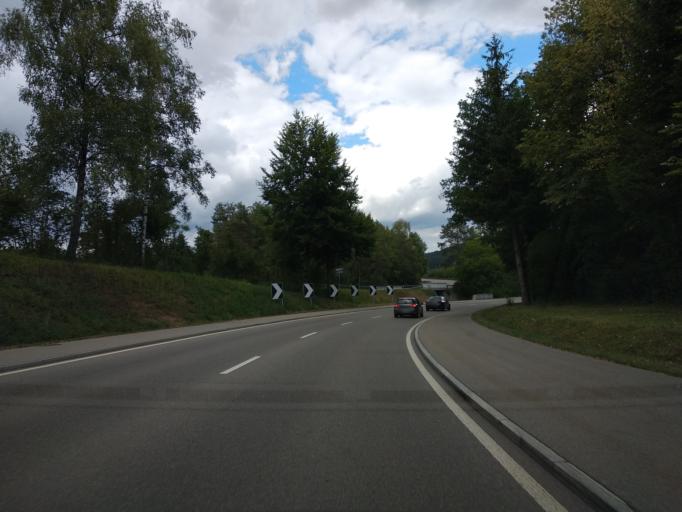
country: CH
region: Zurich
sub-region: Bezirk Pfaeffikon
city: Effretikon / Watt
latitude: 47.4477
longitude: 8.6963
